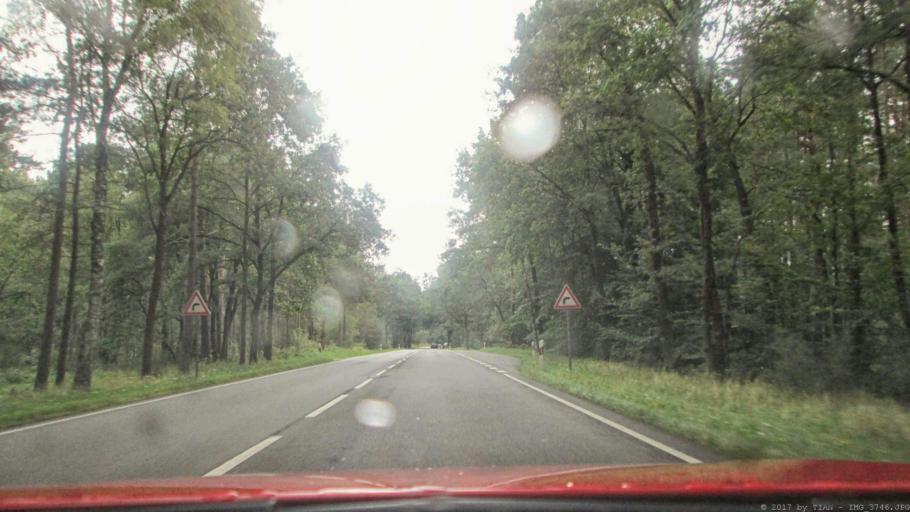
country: DE
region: Lower Saxony
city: Suderburg
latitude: 52.8715
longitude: 10.4946
